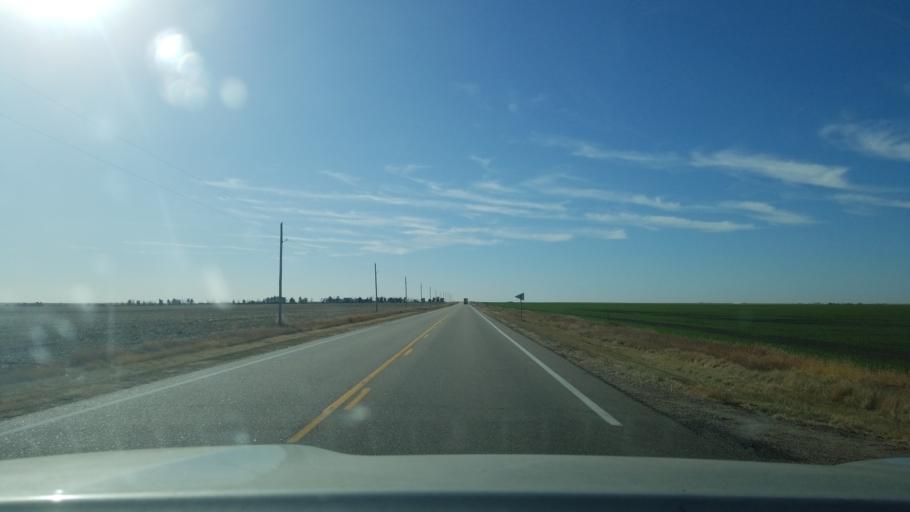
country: US
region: Kansas
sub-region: Ness County
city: Ness City
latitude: 38.3927
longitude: -99.8981
